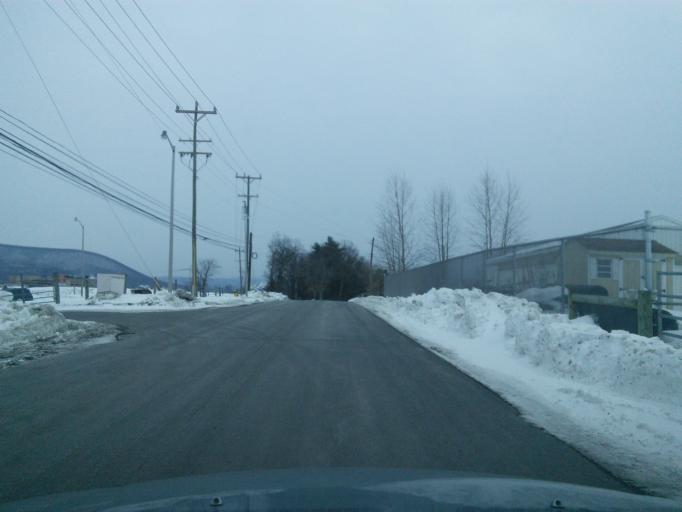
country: US
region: Pennsylvania
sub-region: Centre County
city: Houserville
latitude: 40.8209
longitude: -77.8534
